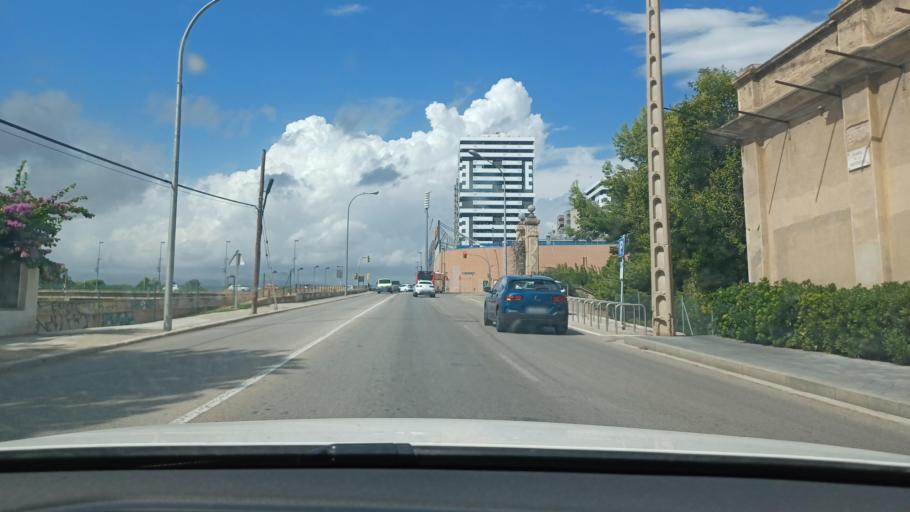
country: ES
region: Catalonia
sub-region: Provincia de Tarragona
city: Tarragona
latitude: 41.1151
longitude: 1.2380
